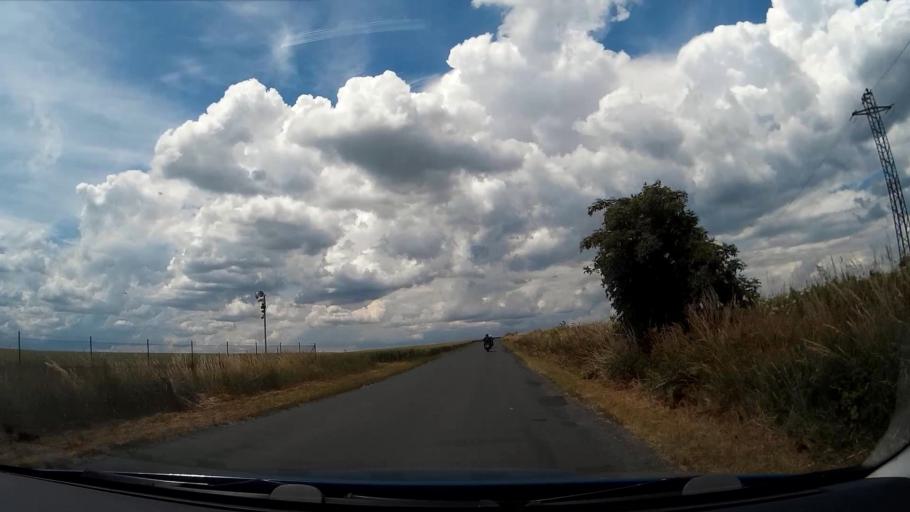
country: CZ
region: South Moravian
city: Orechov
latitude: 49.0858
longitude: 16.5360
